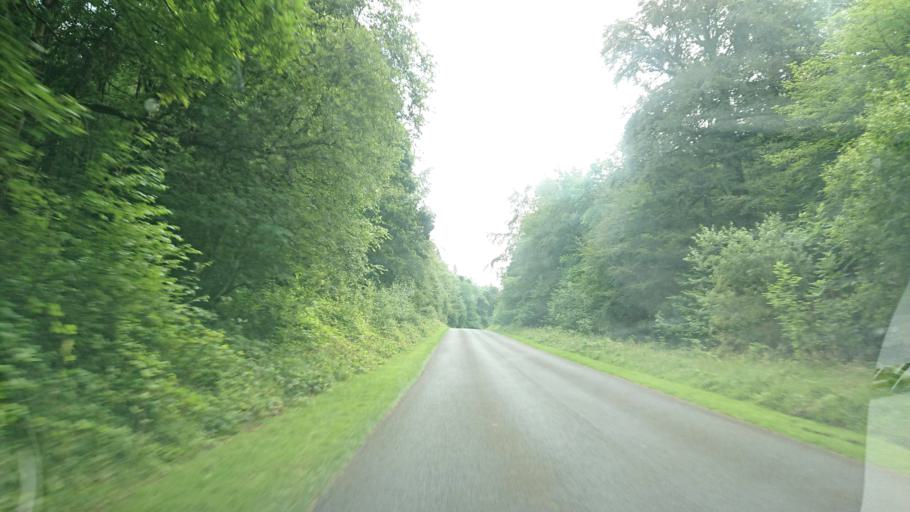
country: IE
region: Connaught
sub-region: Roscommon
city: Boyle
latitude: 53.9775
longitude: -8.2458
